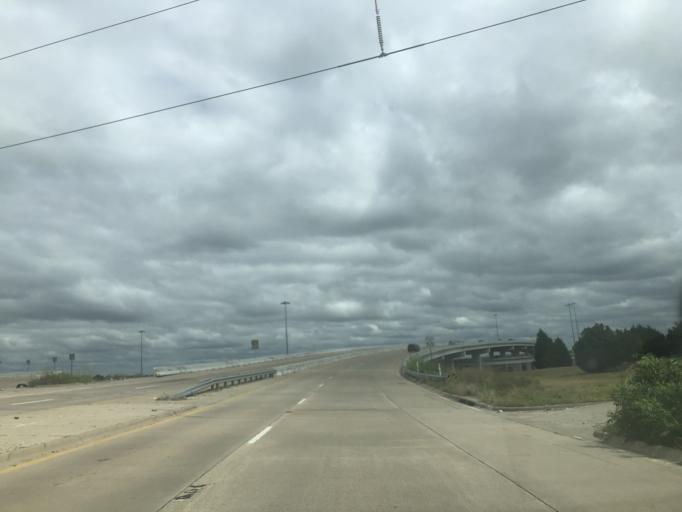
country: US
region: Texas
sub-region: Dallas County
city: Duncanville
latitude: 32.6684
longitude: -96.9468
